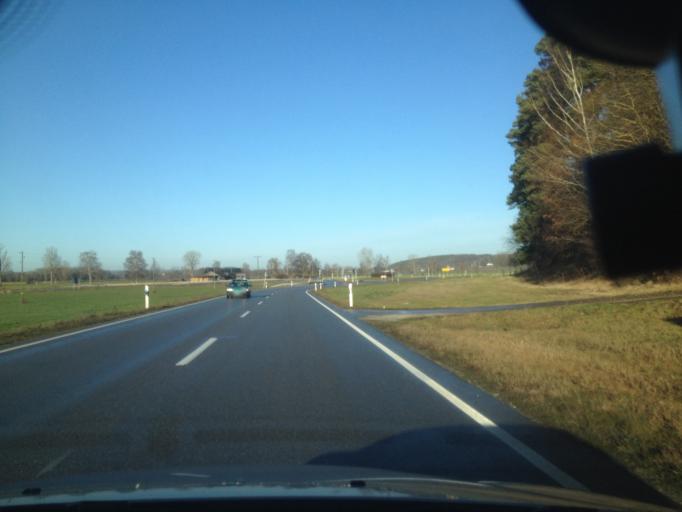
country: DE
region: Bavaria
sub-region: Swabia
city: Haldenwang
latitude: 48.4421
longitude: 10.4285
